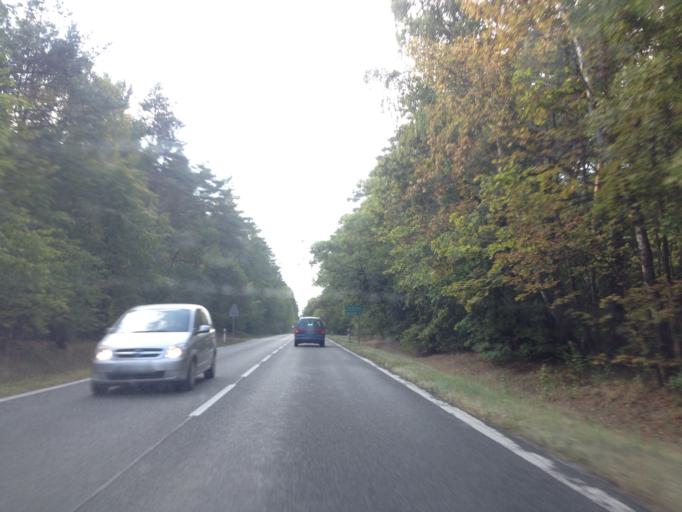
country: PL
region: Kujawsko-Pomorskie
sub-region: Powiat swiecki
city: Lniano
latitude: 53.4719
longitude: 18.1601
